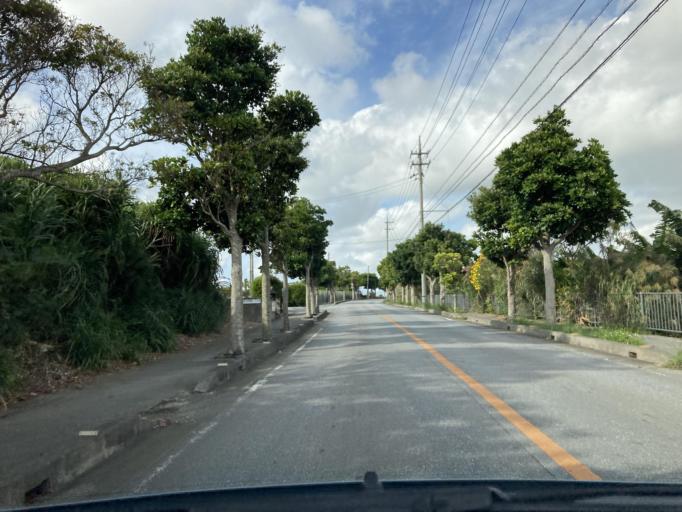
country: JP
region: Okinawa
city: Itoman
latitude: 26.1185
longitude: 127.7157
